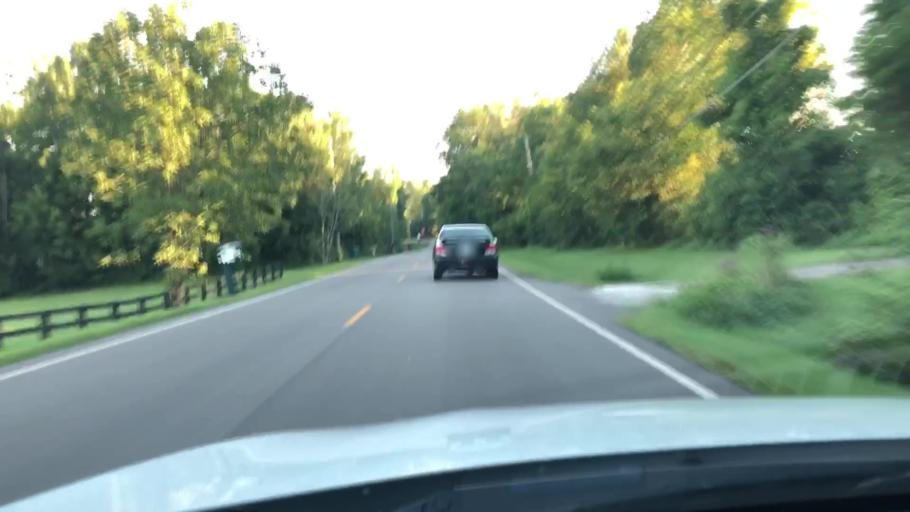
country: US
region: Kentucky
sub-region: Jefferson County
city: Middletown
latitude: 38.2180
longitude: -85.5078
